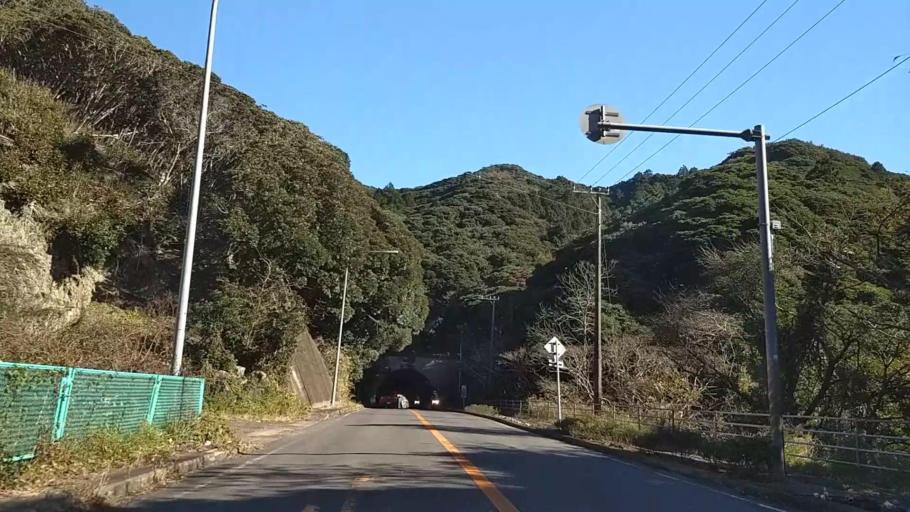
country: JP
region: Chiba
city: Kawaguchi
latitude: 35.1277
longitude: 140.1631
